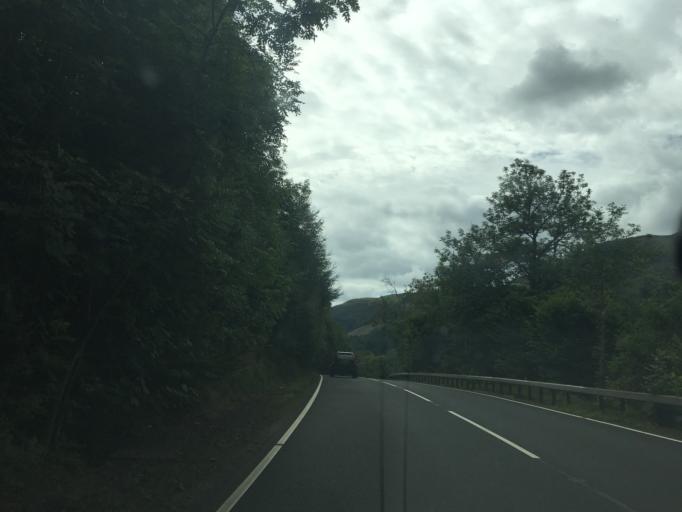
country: GB
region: Scotland
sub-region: Stirling
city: Callander
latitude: 56.2710
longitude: -4.2832
